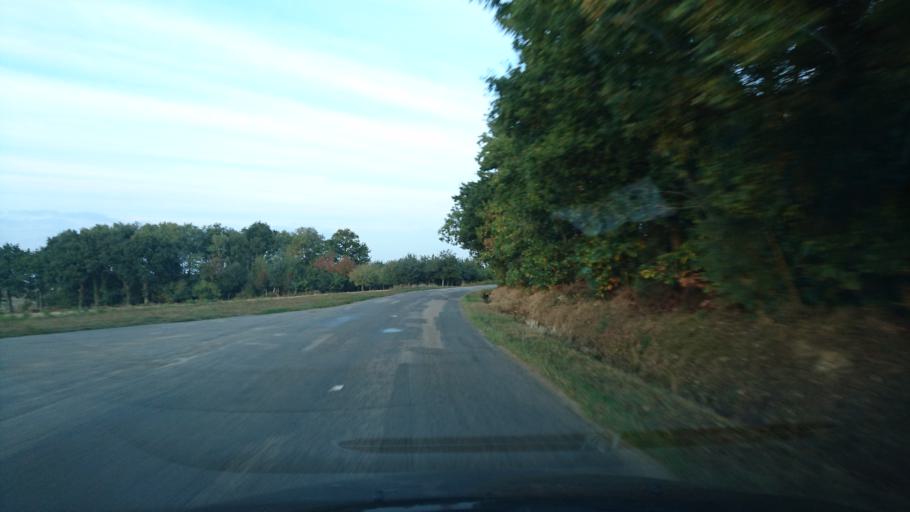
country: FR
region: Brittany
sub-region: Departement du Morbihan
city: Guer
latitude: 47.8825
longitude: -2.0700
